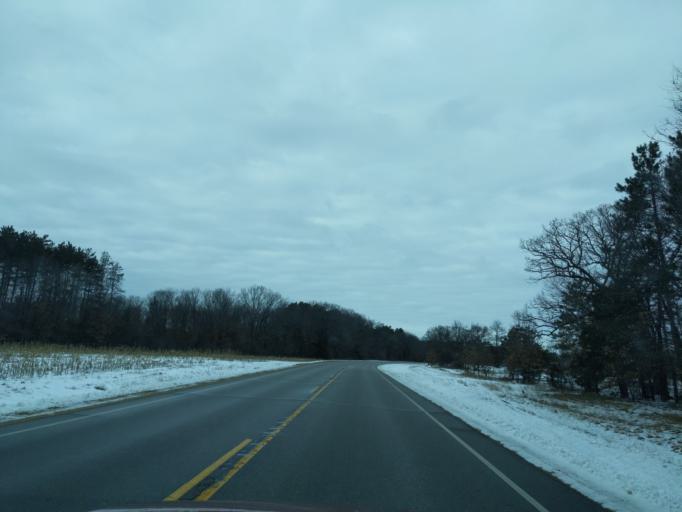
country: US
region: Wisconsin
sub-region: Waushara County
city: Wautoma
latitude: 43.9427
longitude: -89.3161
